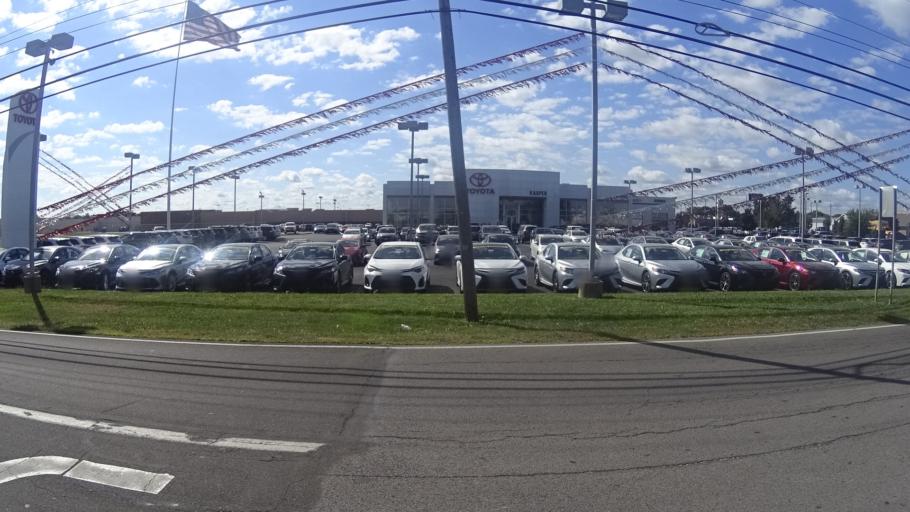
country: US
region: Ohio
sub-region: Erie County
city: Sandusky
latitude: 41.4224
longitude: -82.6758
